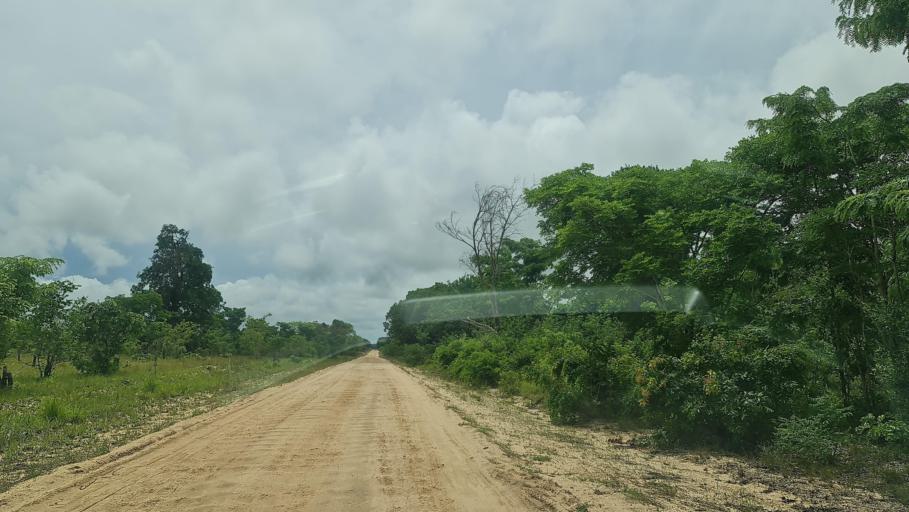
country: MZ
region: Zambezia
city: Quelimane
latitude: -17.2572
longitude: 37.2279
